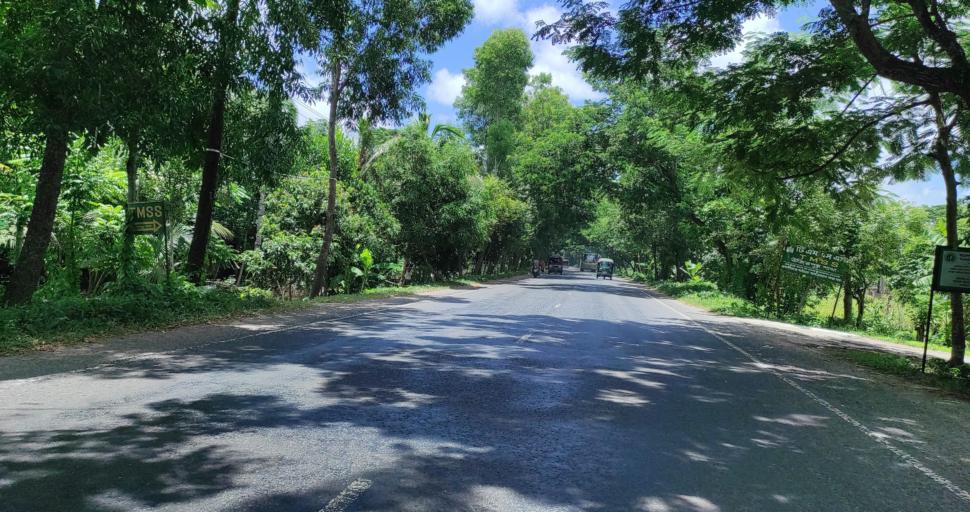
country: BD
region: Barisal
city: Gaurnadi
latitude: 22.8347
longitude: 90.2540
